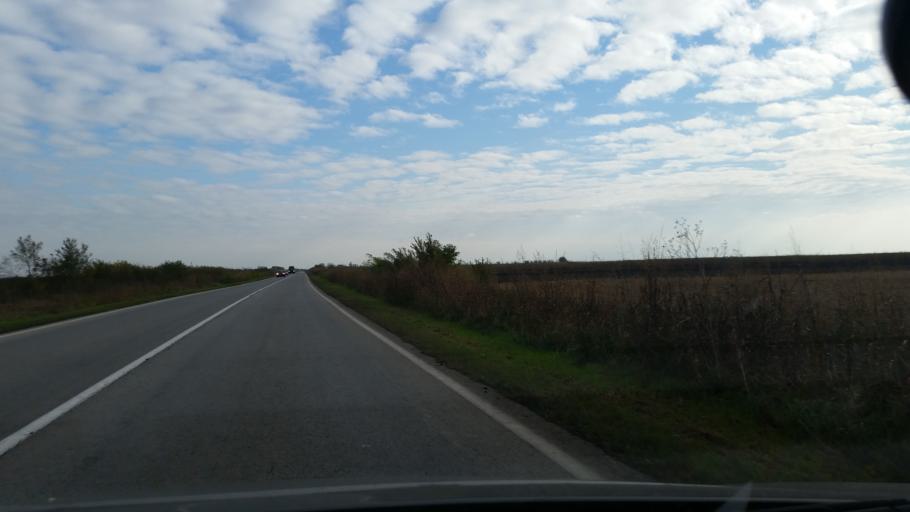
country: RS
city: Elemir
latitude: 45.4522
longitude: 20.3555
